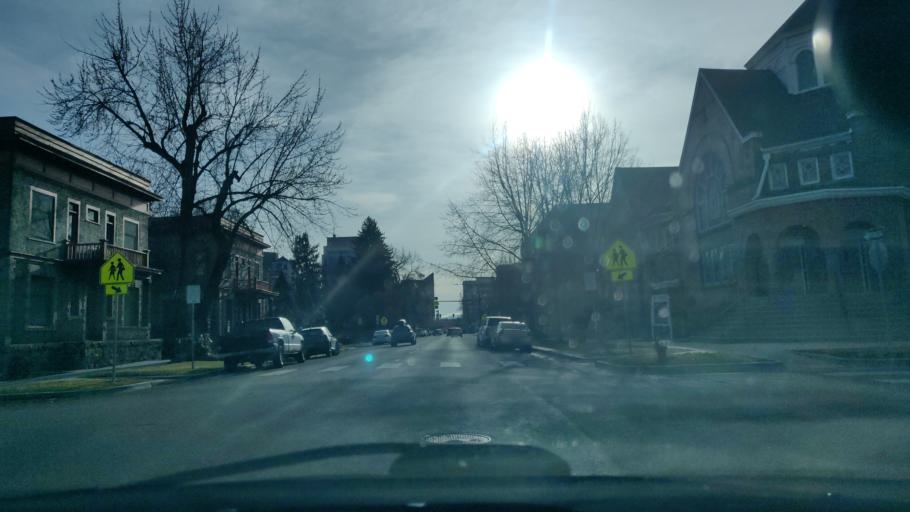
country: US
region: Idaho
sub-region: Ada County
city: Boise
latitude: 43.6209
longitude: -116.2002
